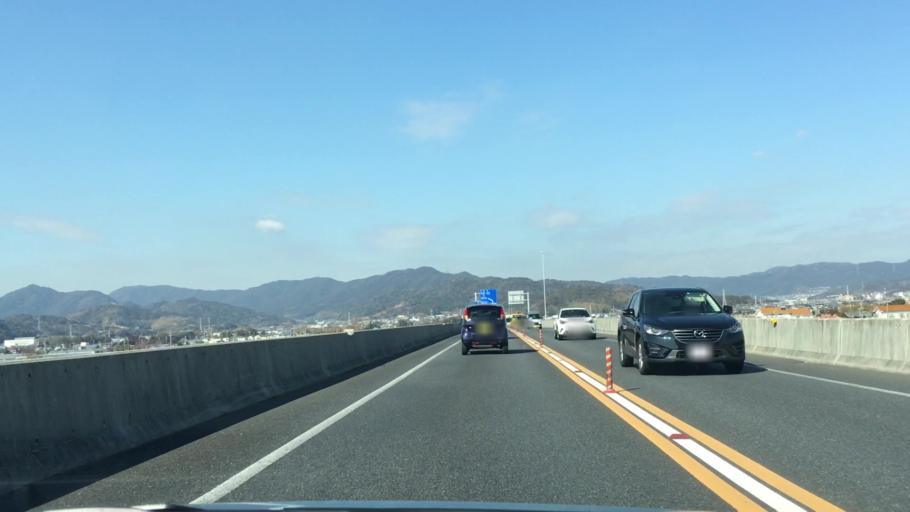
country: JP
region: Aichi
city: Kozakai-cho
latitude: 34.8123
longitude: 137.3341
